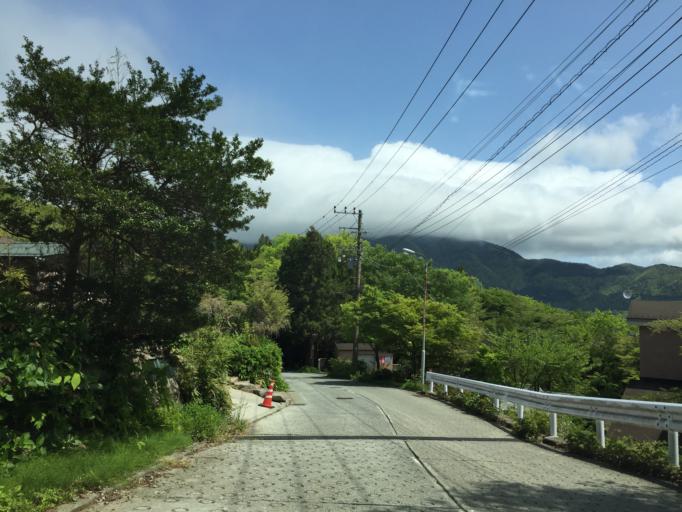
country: JP
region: Kanagawa
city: Hakone
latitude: 35.2460
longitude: 139.0379
